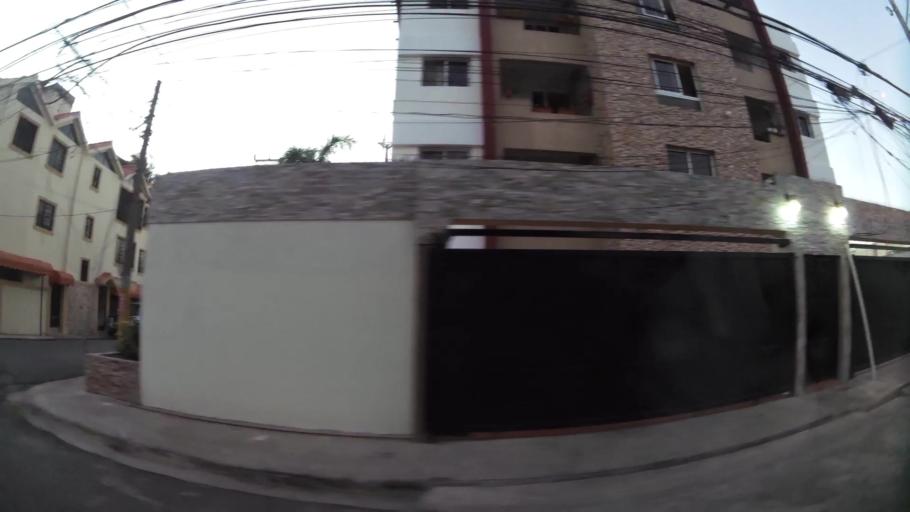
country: DO
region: Santo Domingo
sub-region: Santo Domingo
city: Santo Domingo Este
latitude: 18.4946
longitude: -69.8389
